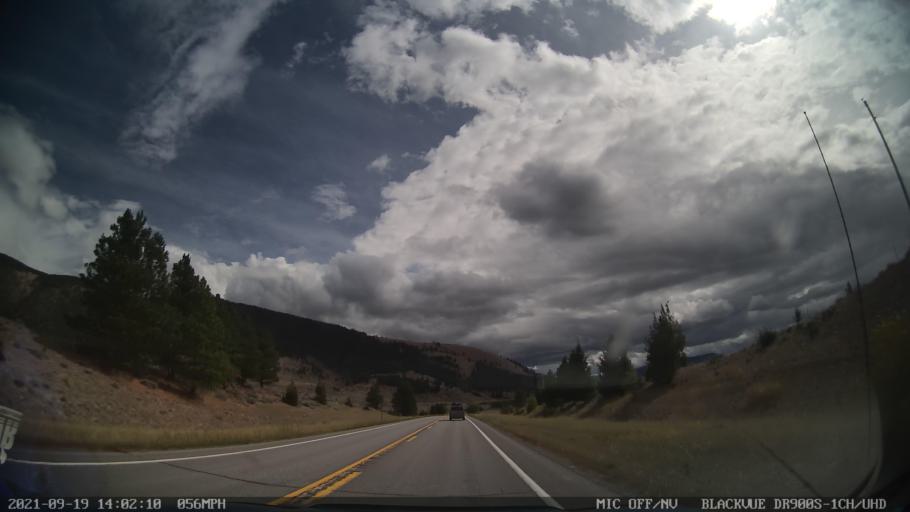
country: US
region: Montana
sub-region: Lewis and Clark County
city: Lincoln
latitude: 46.9710
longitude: -112.9704
